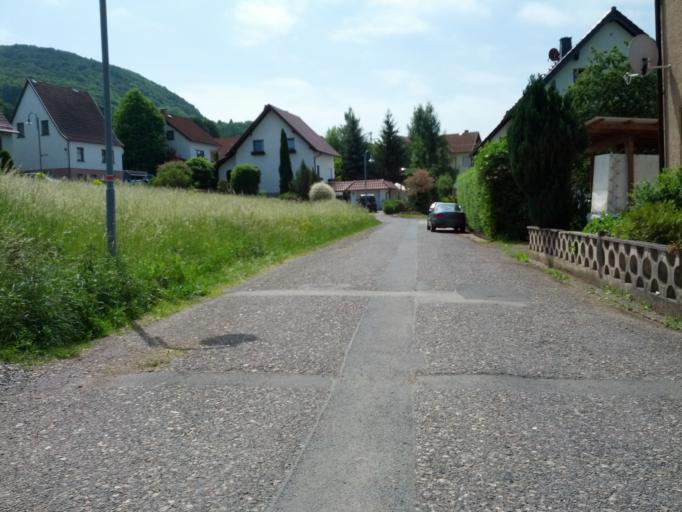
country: DE
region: Thuringia
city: Urnshausen
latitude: 50.7315
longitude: 10.1734
